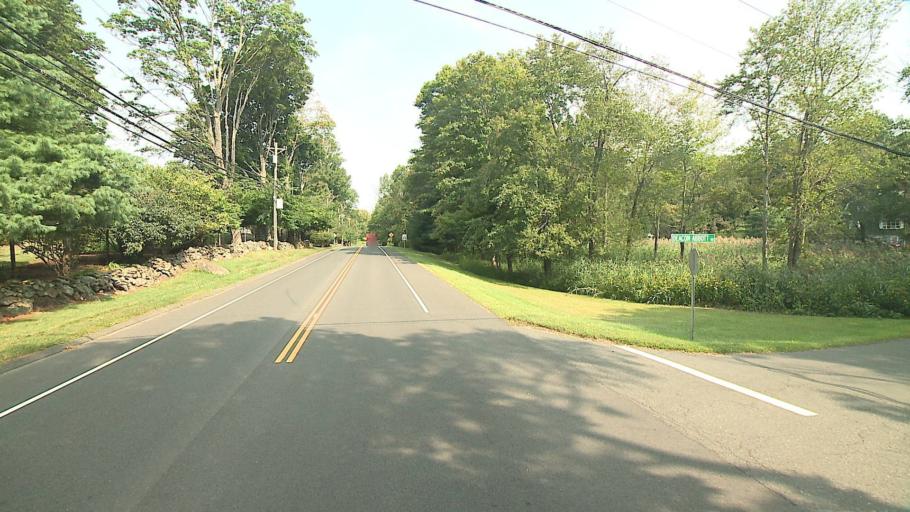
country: US
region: Connecticut
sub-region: Fairfield County
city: Bethel
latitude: 41.3119
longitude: -73.3850
